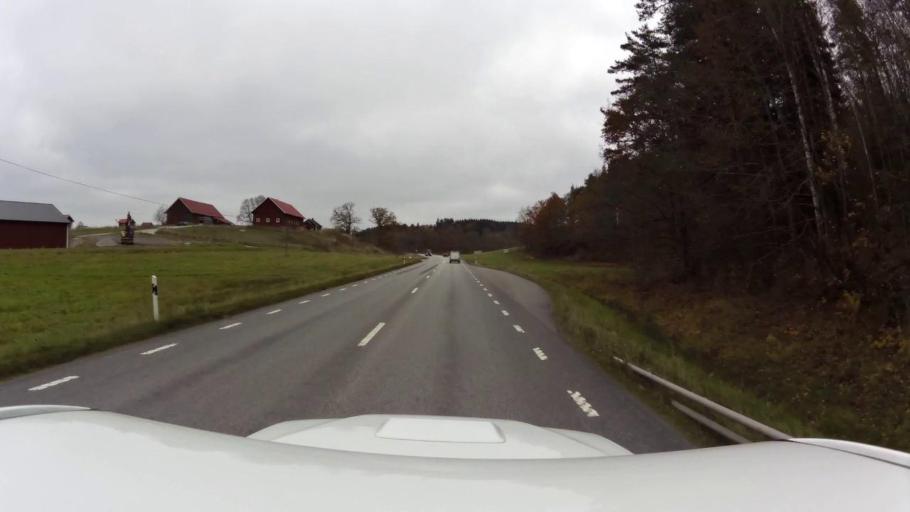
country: SE
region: OEstergoetland
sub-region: Kinda Kommun
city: Rimforsa
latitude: 58.1794
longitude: 15.6740
